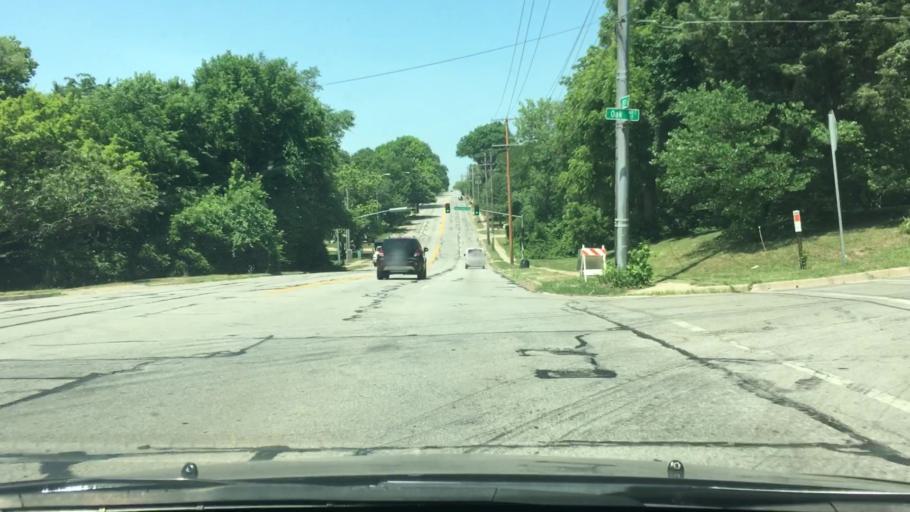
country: US
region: Kansas
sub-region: Johnson County
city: Leawood
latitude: 38.9739
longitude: -94.5858
